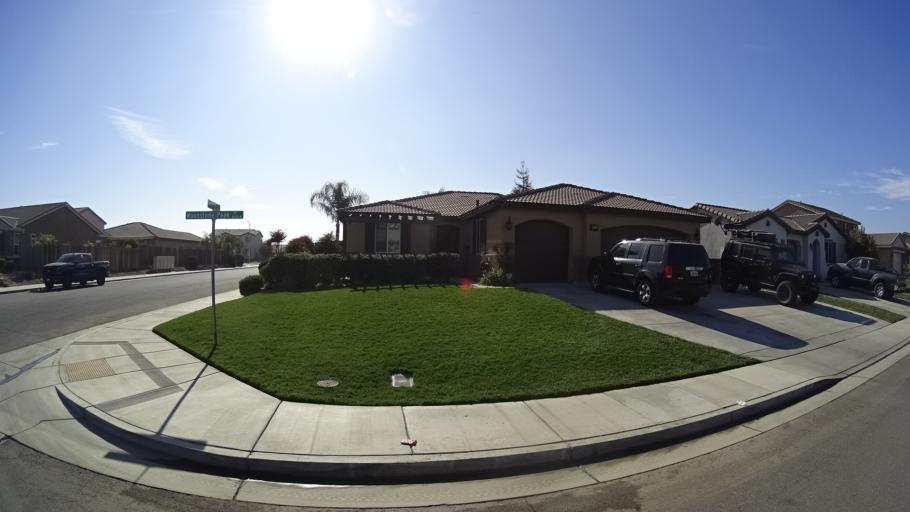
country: US
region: California
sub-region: Kern County
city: Greenfield
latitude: 35.2756
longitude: -119.0681
